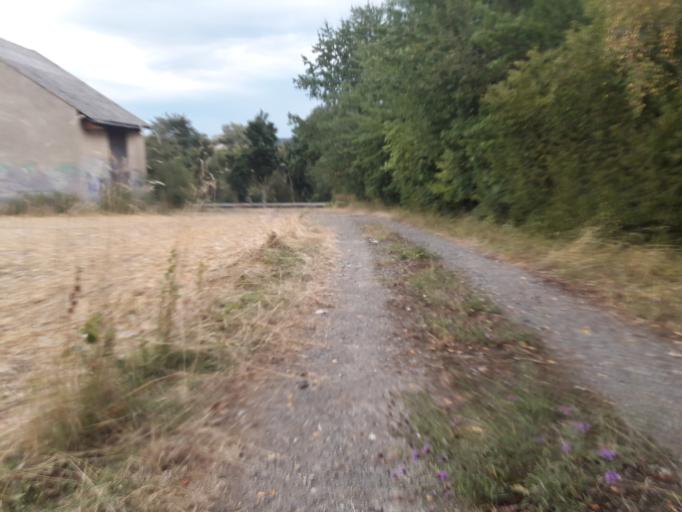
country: DE
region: North Rhine-Westphalia
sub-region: Regierungsbezirk Detmold
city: Paderborn
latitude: 51.6781
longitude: 8.7310
